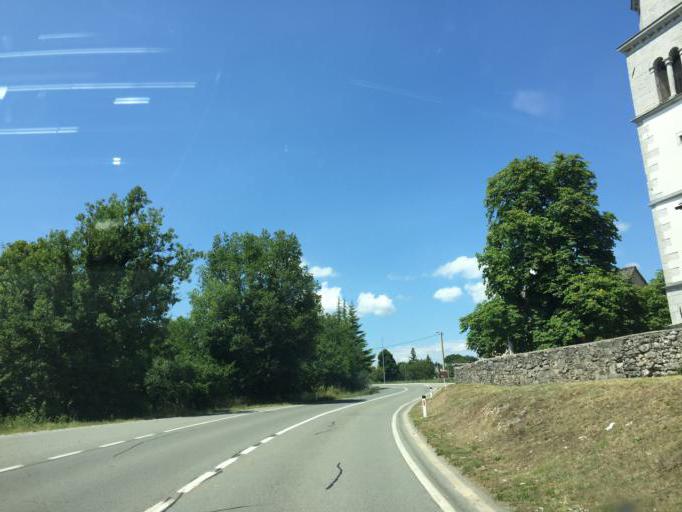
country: SI
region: Sezana
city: Sezana
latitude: 45.7408
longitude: 13.8650
